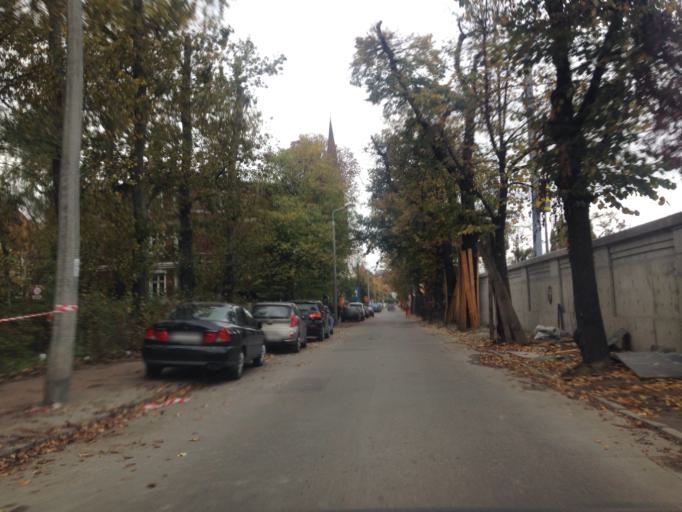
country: PL
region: Pomeranian Voivodeship
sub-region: Gdansk
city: Gdansk
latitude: 54.3792
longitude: 18.6121
